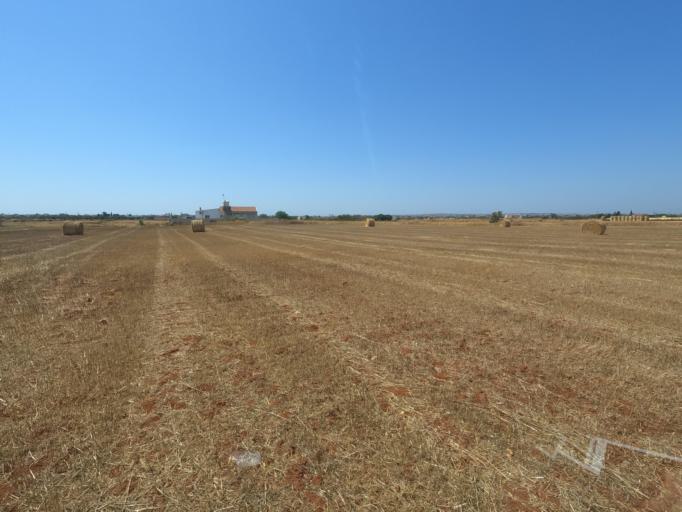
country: CY
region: Ammochostos
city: Liopetri
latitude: 35.0210
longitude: 33.8829
